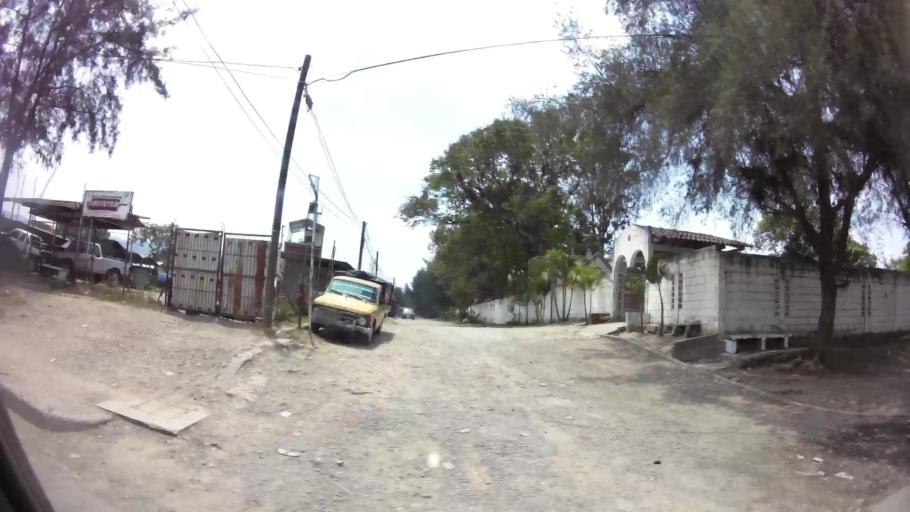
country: HN
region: Comayagua
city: Siguatepeque
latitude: 14.5913
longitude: -87.8325
